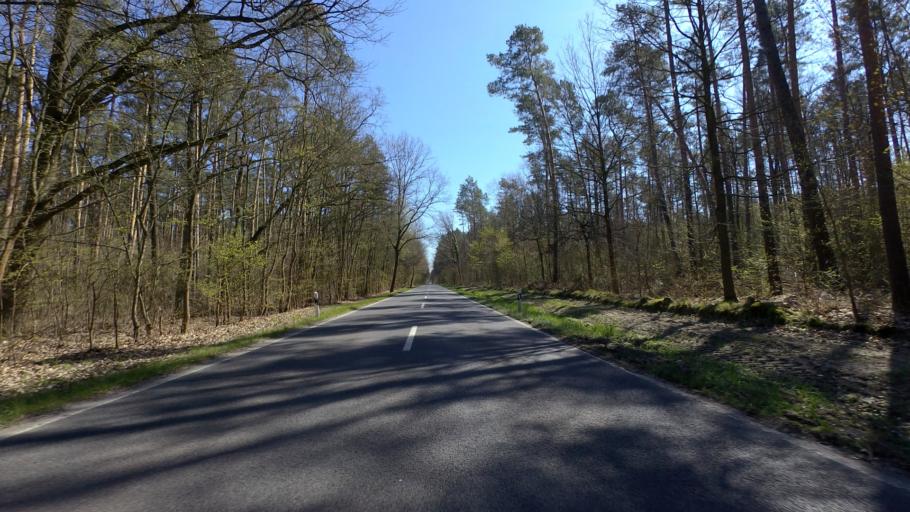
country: DE
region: Brandenburg
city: Schulzendorf
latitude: 52.3399
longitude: 13.5791
